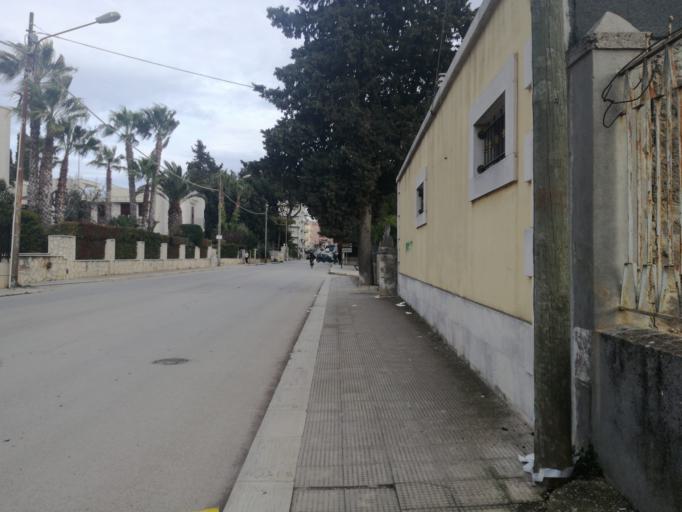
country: IT
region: Apulia
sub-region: Provincia di Bari
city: Ruvo di Puglia
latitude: 41.1192
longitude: 16.4758
